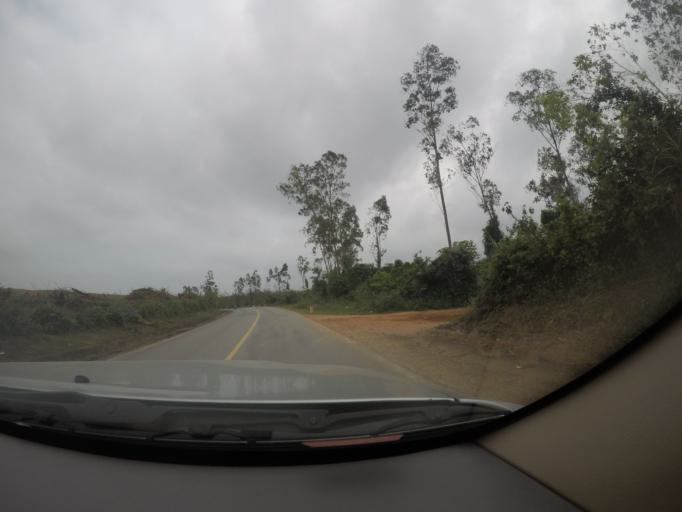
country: VN
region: Quang Binh
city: Hoan Lao
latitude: 17.4927
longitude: 106.5126
